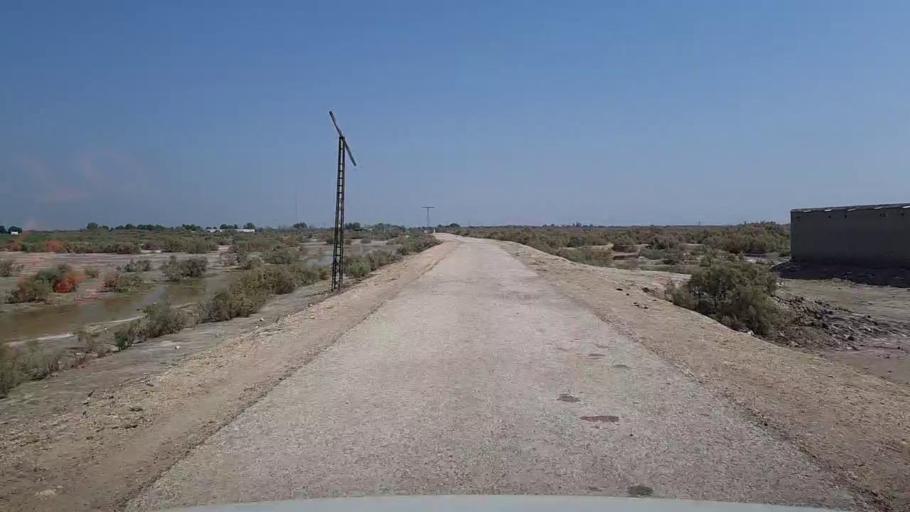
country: PK
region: Sindh
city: Kandhkot
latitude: 28.3036
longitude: 69.3467
